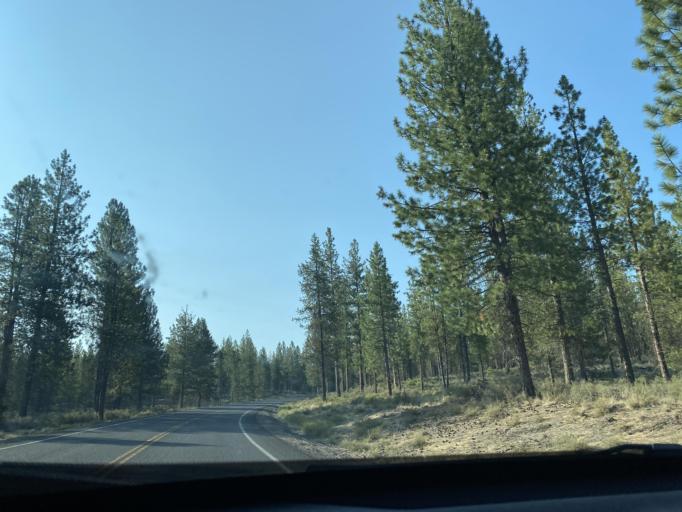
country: US
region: Oregon
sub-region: Deschutes County
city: La Pine
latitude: 43.7255
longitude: -121.4160
